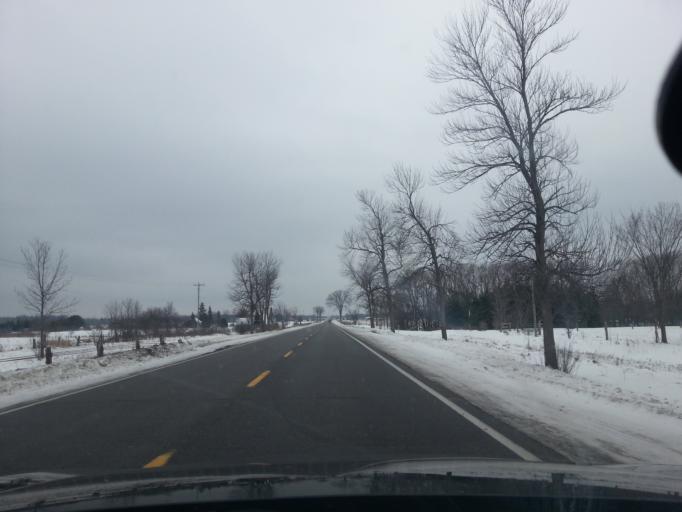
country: CA
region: Ontario
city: Bells Corners
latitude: 45.3239
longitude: -76.0402
